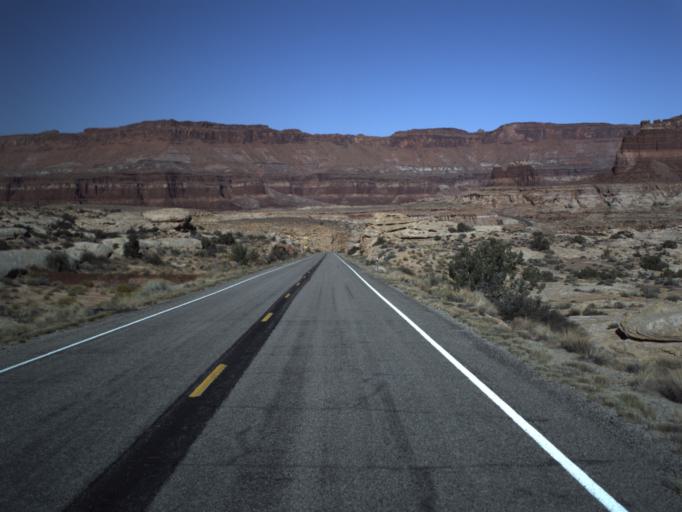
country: US
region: Utah
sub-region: San Juan County
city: Blanding
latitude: 37.8829
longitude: -110.3596
